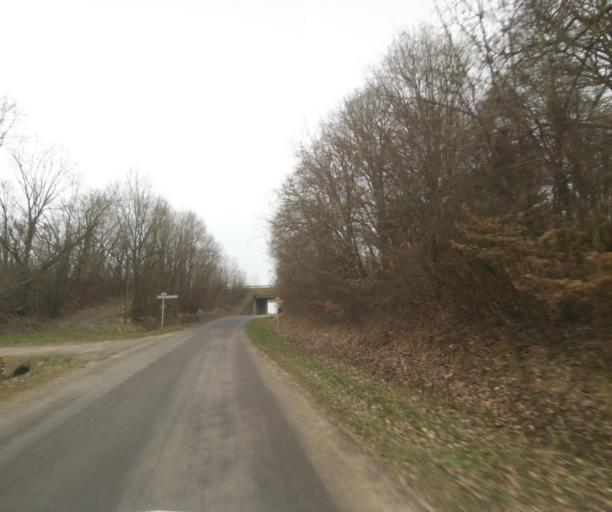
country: FR
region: Champagne-Ardenne
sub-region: Departement de la Haute-Marne
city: Bienville
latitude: 48.5798
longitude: 5.0335
